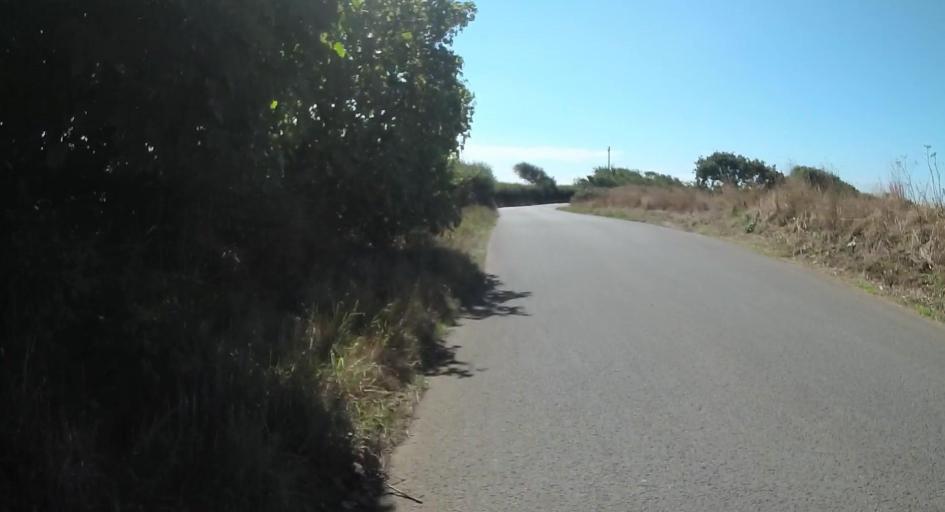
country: GB
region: England
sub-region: Isle of Wight
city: Chale
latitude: 50.6154
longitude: -1.3224
